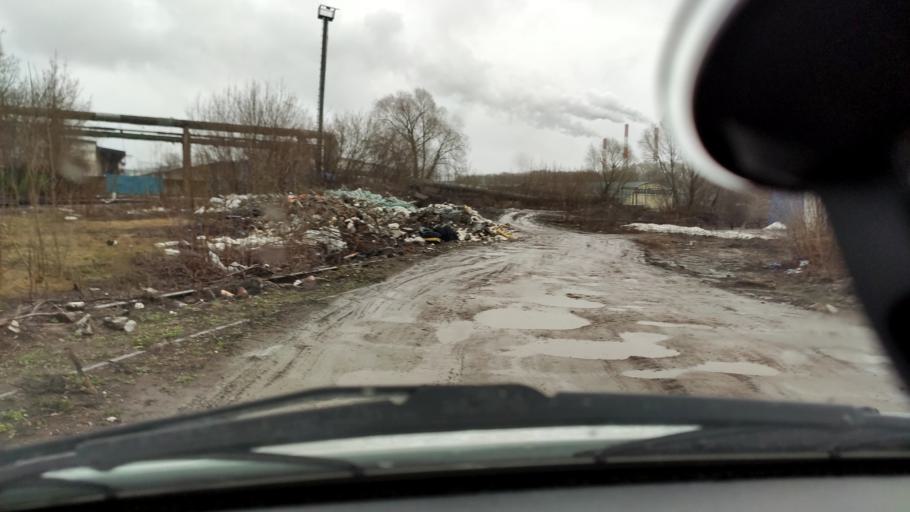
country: RU
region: Bashkortostan
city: Ufa
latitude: 54.7984
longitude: 56.0996
